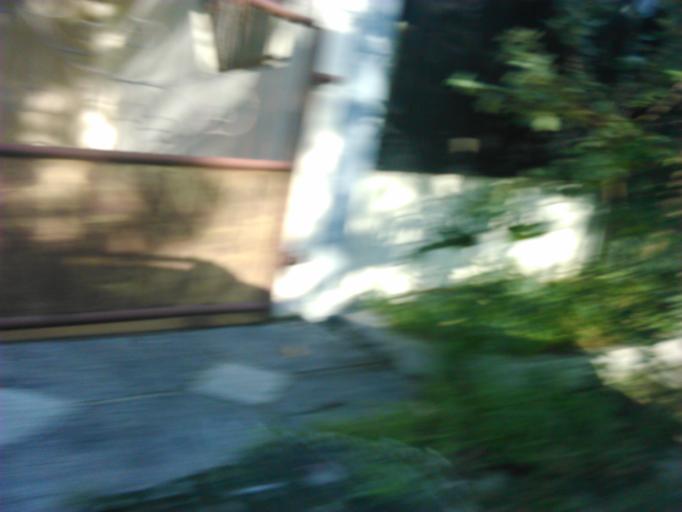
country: ID
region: East Java
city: Wonorejo
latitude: -7.2899
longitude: 112.8025
